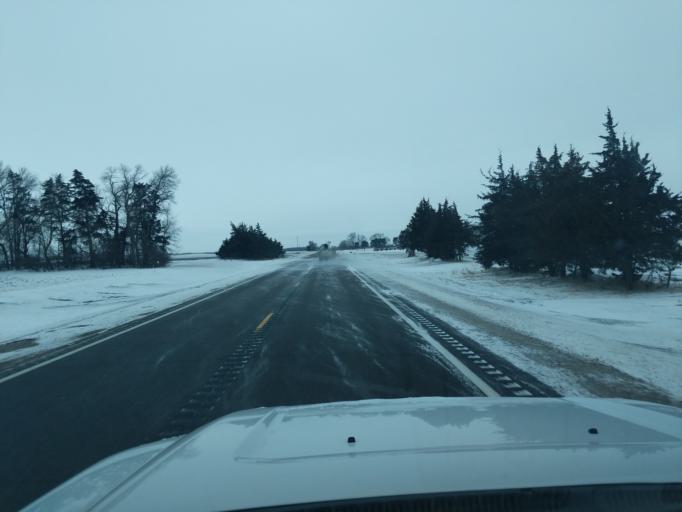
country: US
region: Minnesota
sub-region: Redwood County
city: Redwood Falls
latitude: 44.5903
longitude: -94.9945
